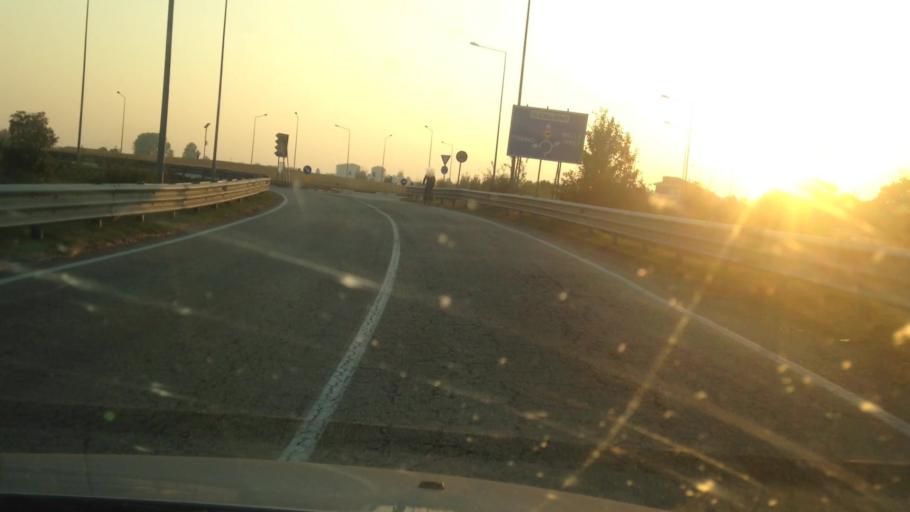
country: IT
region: Piedmont
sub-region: Provincia di Vercelli
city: Cigliano
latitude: 45.3134
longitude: 8.0422
